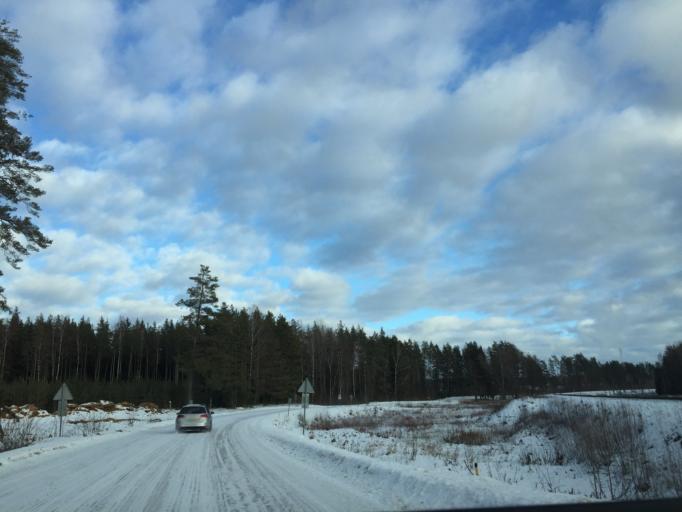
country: LV
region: Ogre
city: Jumprava
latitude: 56.5625
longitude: 24.9124
